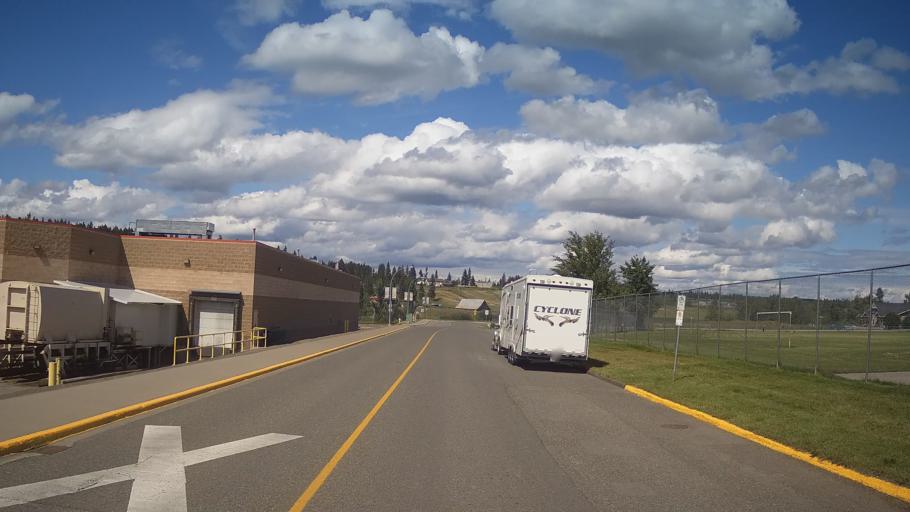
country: CA
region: British Columbia
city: Cache Creek
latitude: 51.6474
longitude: -121.2944
